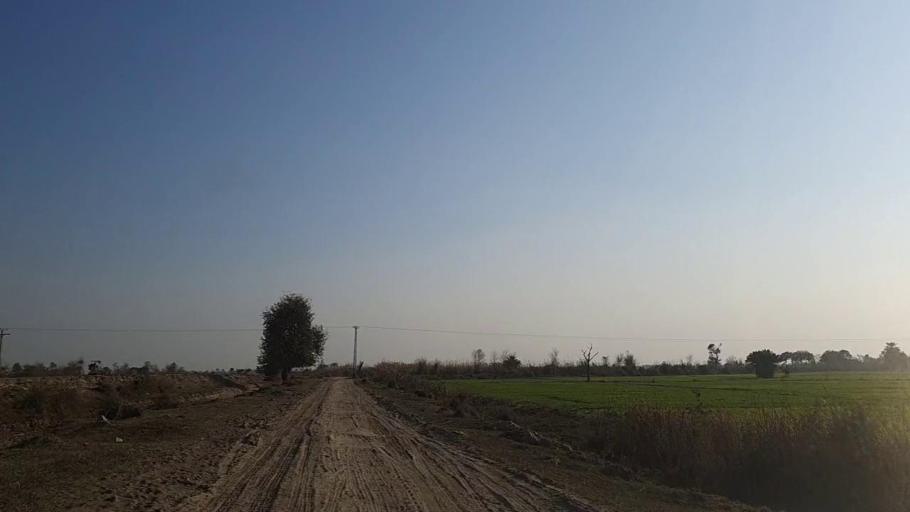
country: PK
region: Sindh
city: Daur
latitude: 26.4369
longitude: 68.3522
